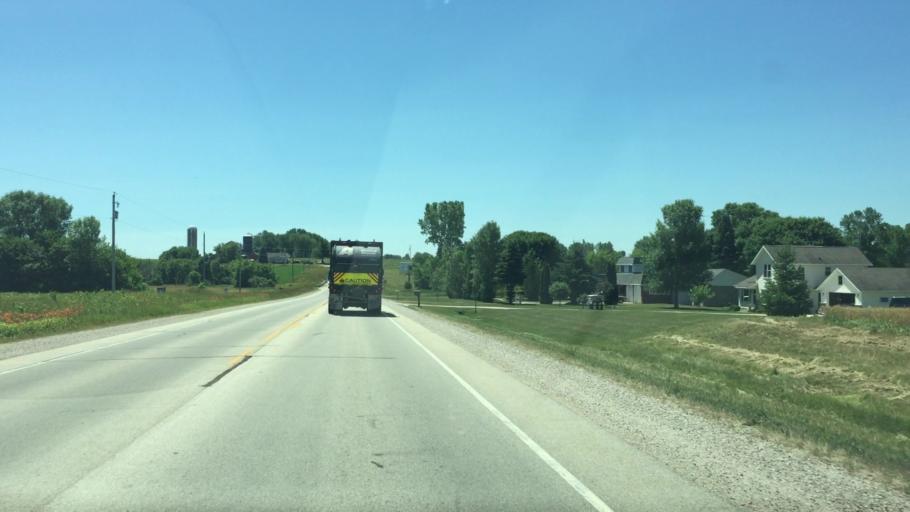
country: US
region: Wisconsin
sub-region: Calumet County
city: Chilton
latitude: 44.0630
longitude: -88.1632
